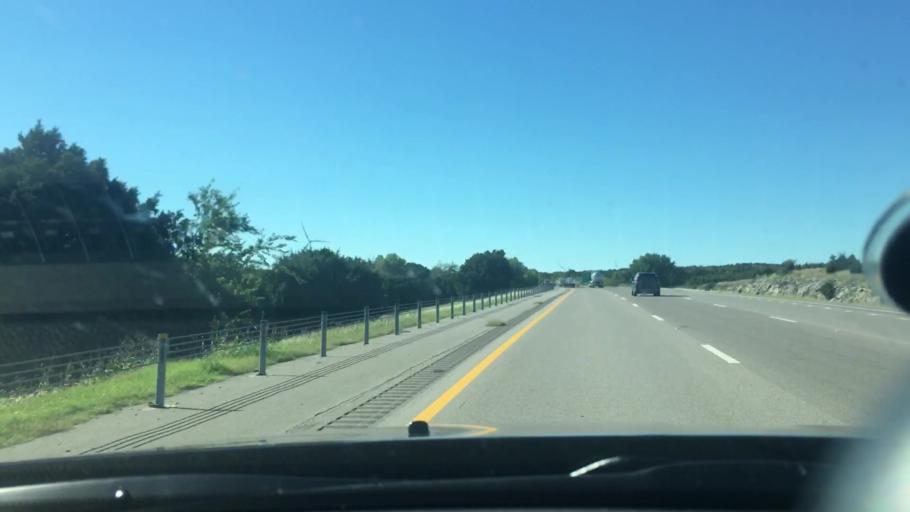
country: US
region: Oklahoma
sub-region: Murray County
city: Davis
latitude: 34.4210
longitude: -97.1359
